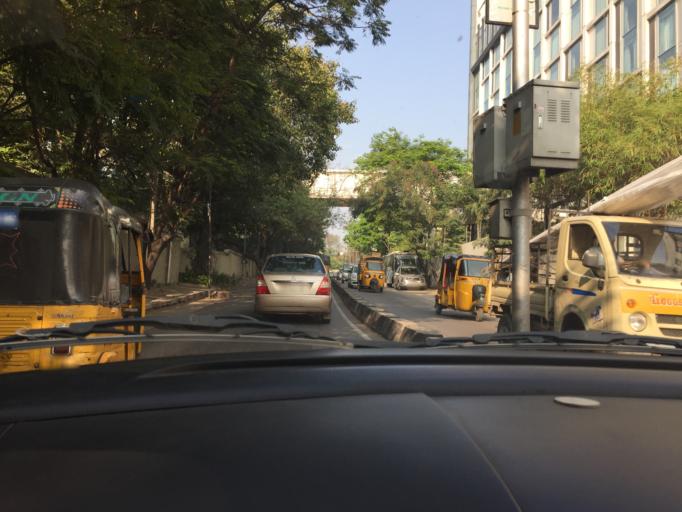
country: IN
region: Telangana
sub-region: Hyderabad
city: Malkajgiri
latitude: 17.4234
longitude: 78.4871
